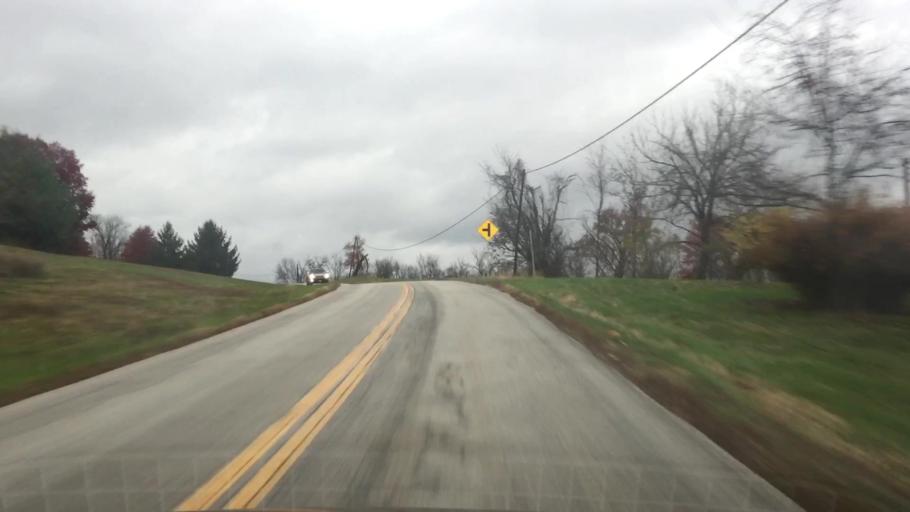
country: US
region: Missouri
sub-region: Boone County
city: Columbia
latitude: 38.9148
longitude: -92.4686
